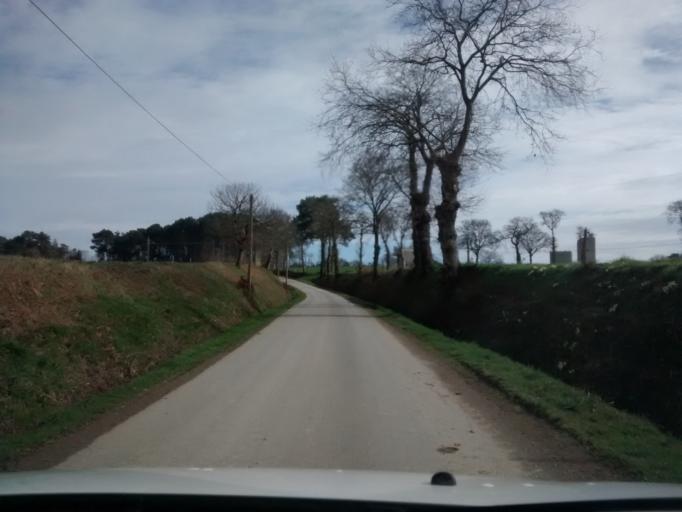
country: FR
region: Brittany
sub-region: Departement d'Ille-et-Vilaine
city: Liffre
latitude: 48.1950
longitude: -1.4900
